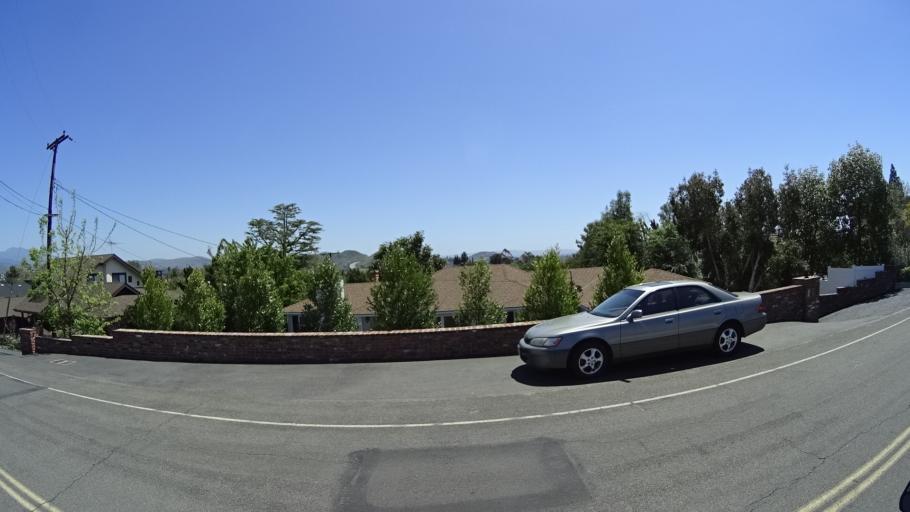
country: US
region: California
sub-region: Orange County
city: Villa Park
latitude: 33.8230
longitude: -117.7995
